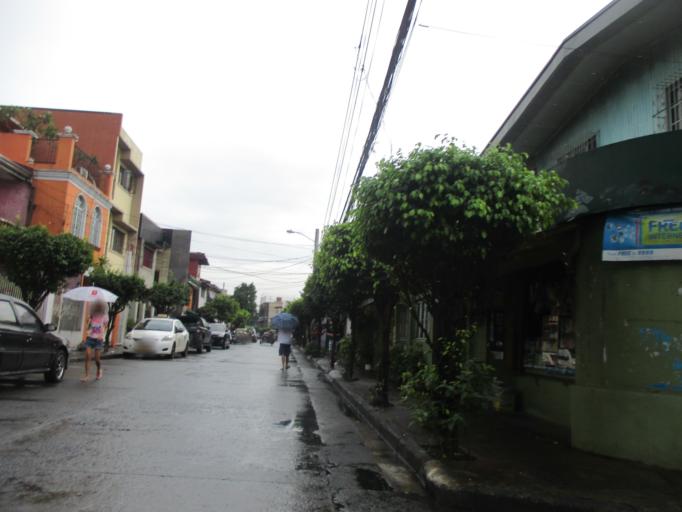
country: PH
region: Metro Manila
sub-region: Marikina
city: Calumpang
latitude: 14.6224
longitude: 121.0945
